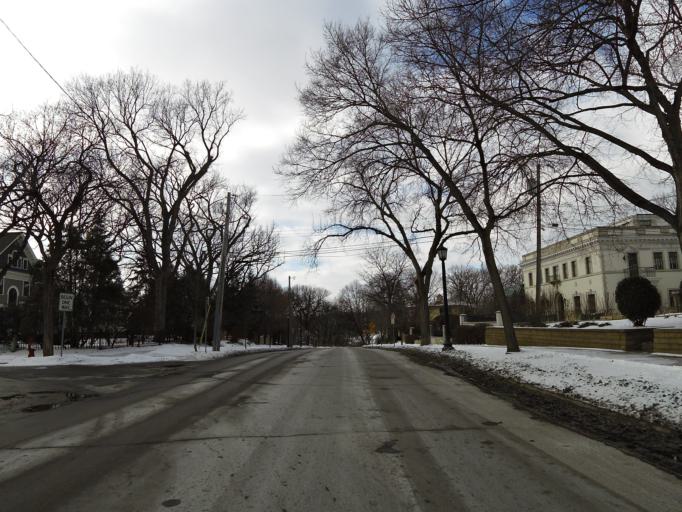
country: US
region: Minnesota
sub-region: Hennepin County
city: Minneapolis
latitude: 44.9627
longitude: -93.3009
